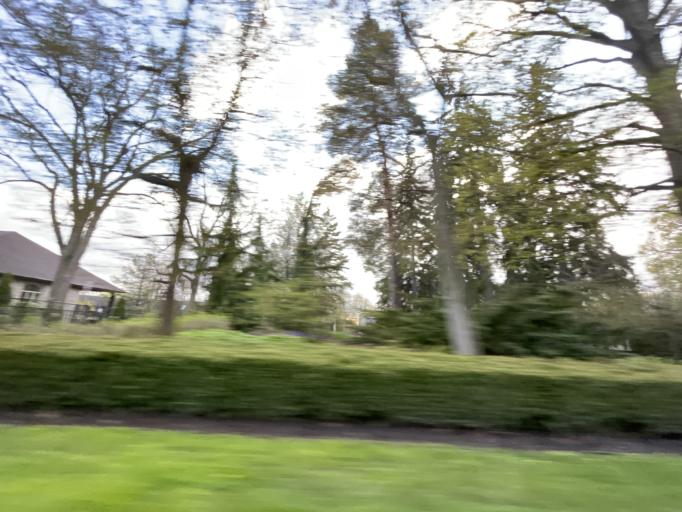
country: CA
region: Ontario
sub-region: Wellington County
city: Guelph
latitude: 43.5510
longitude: -80.2446
